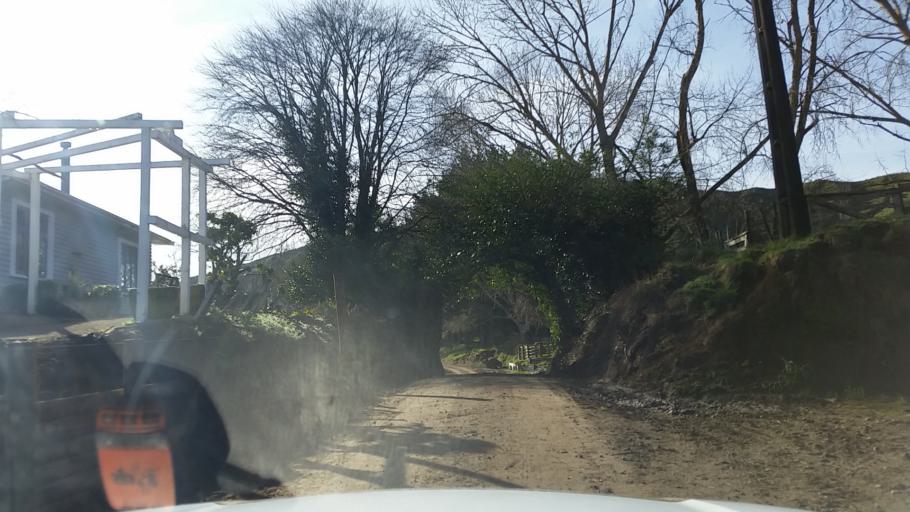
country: NZ
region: Taranaki
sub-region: South Taranaki District
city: Eltham
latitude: -39.3192
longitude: 174.5308
